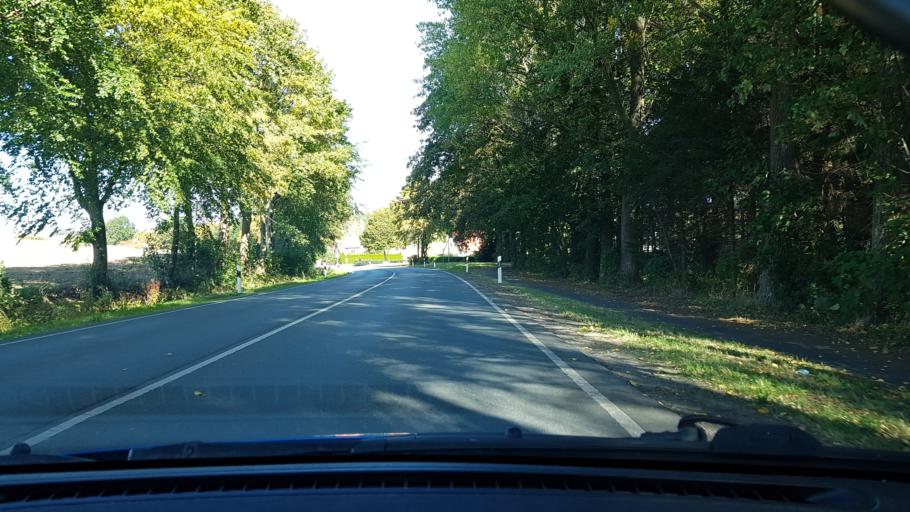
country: DE
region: Lower Saxony
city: Bad Munder am Deister
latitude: 52.2253
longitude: 9.4356
